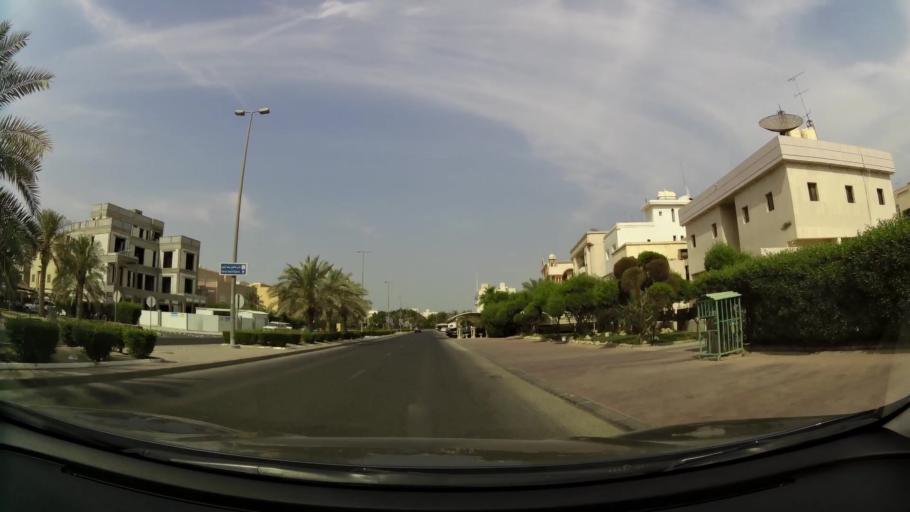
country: KW
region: Al Asimah
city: Ash Shamiyah
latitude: 29.3412
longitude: 47.9761
